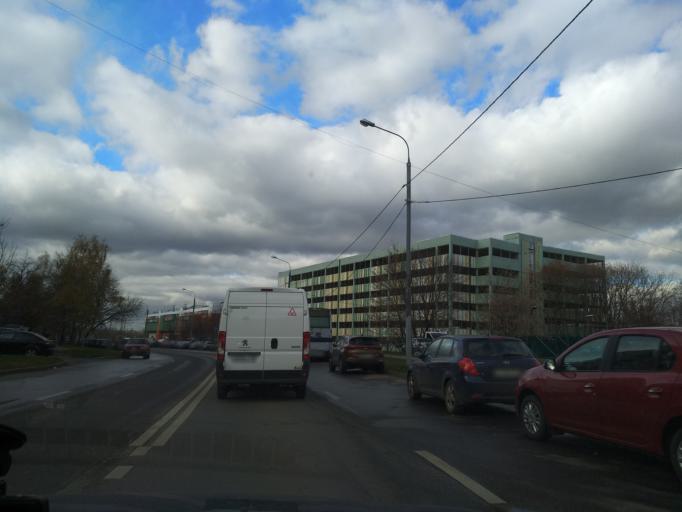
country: RU
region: Moscow
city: Kozeyevo
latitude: 55.8971
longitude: 37.6326
